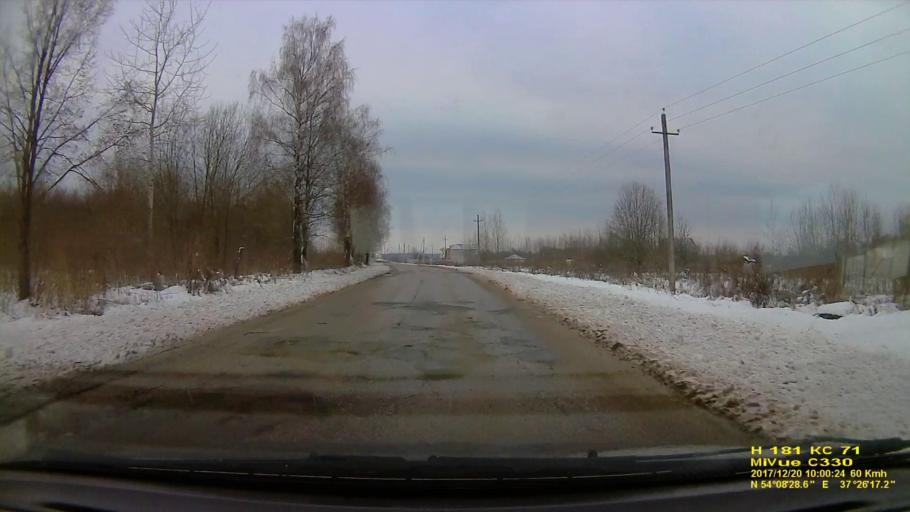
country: RU
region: Tula
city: Kosaya Gora
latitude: 54.1411
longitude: 37.4381
